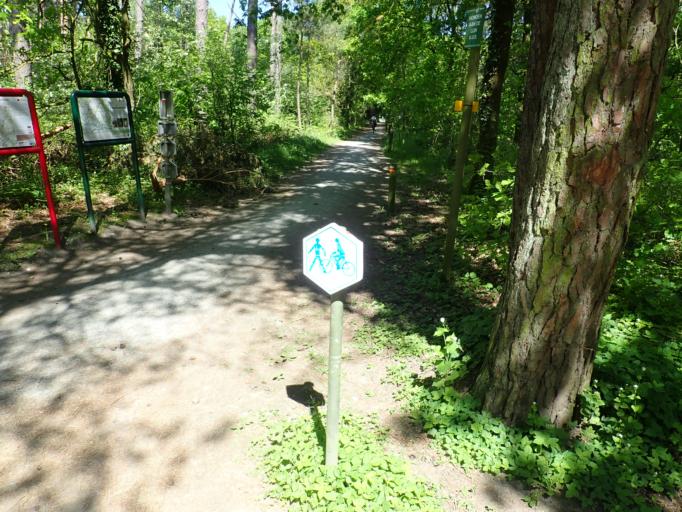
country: BE
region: Flanders
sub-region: Provincie Antwerpen
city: Zandhoven
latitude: 51.2433
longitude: 4.6764
